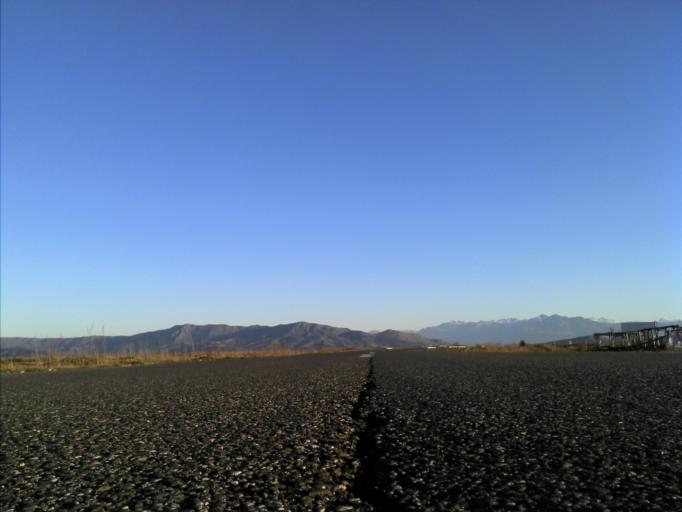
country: AL
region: Shkoder
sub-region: Rrethi i Shkodres
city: Dajc
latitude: 41.9392
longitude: 19.4441
